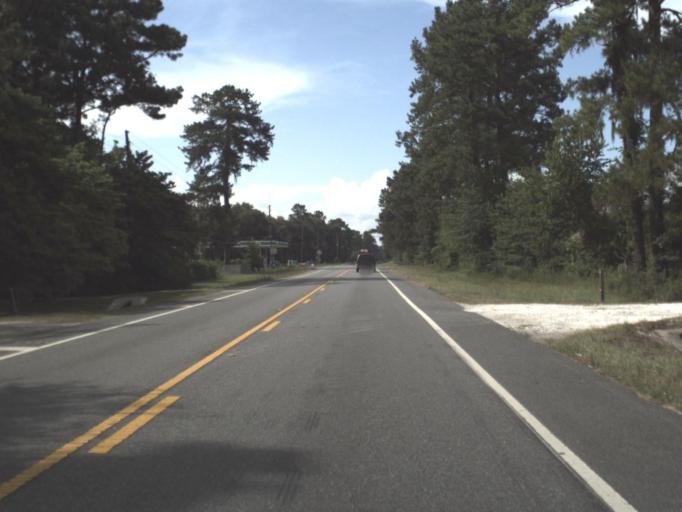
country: US
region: Florida
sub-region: Taylor County
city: Perry
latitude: 30.1634
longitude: -83.5948
